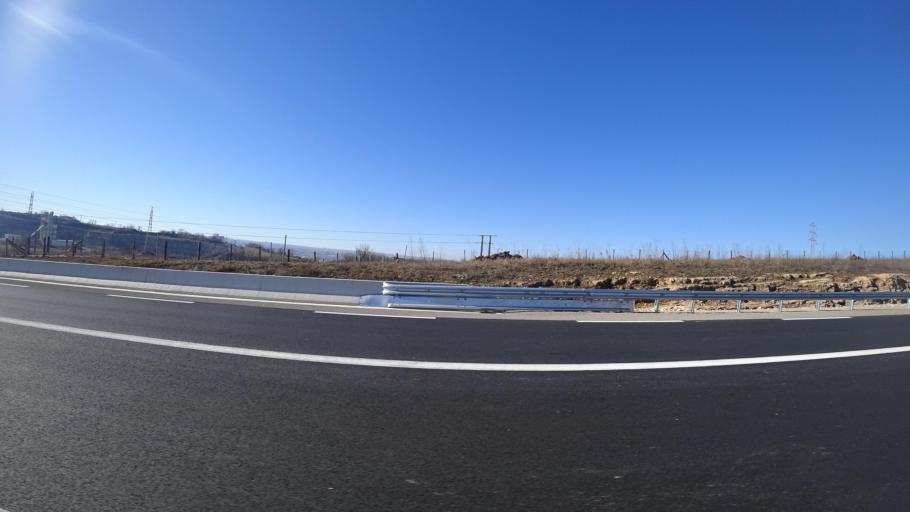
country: FR
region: Midi-Pyrenees
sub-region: Departement de l'Aveyron
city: Sebazac-Concoures
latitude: 44.3870
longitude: 2.6143
